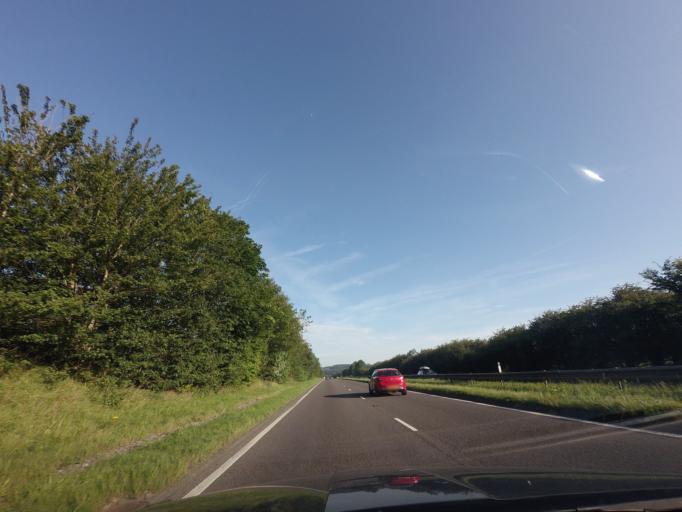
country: GB
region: England
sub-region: Derbyshire
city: Chesterfield
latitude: 53.2174
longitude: -1.3958
